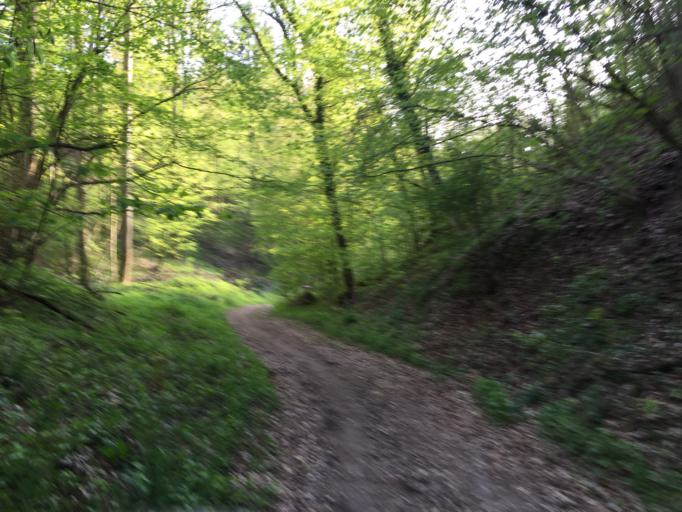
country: DE
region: Baden-Wuerttemberg
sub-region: Karlsruhe Region
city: Weinheim
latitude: 49.5151
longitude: 8.6798
